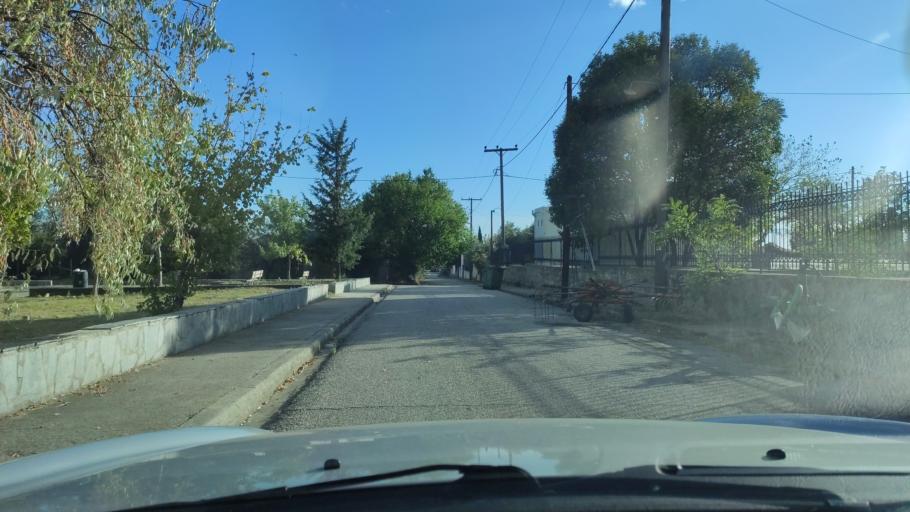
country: GR
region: East Macedonia and Thrace
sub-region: Nomos Xanthis
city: Selero
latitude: 41.1246
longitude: 25.0642
